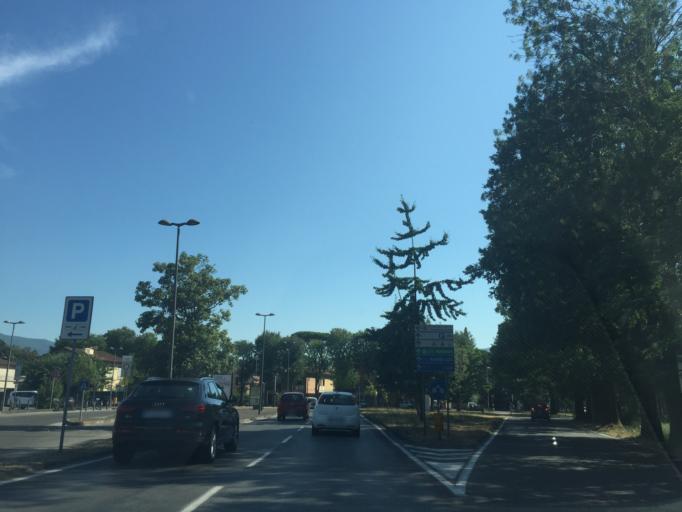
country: IT
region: Tuscany
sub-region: Provincia di Lucca
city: Lucca
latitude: 43.8465
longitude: 10.4944
